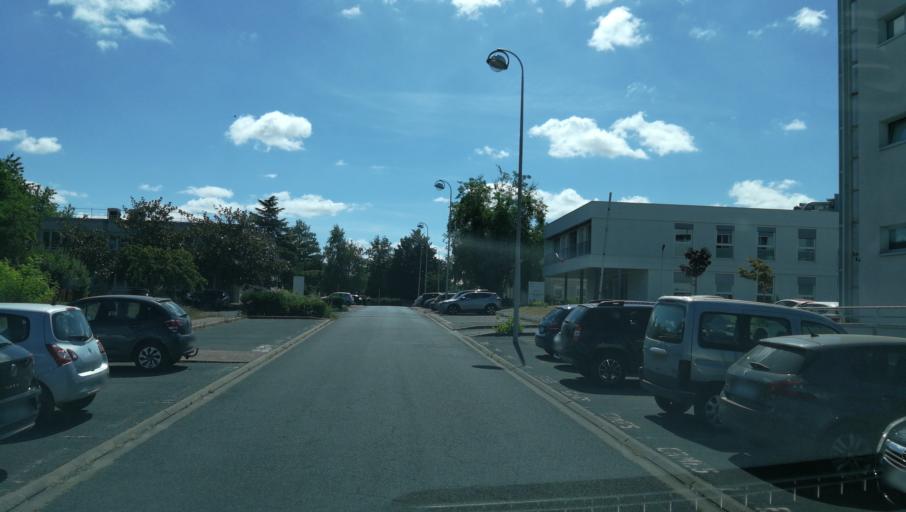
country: FR
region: Centre
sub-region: Departement du Loiret
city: Saint-Cyr-en-Val
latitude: 47.8443
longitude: 1.9406
